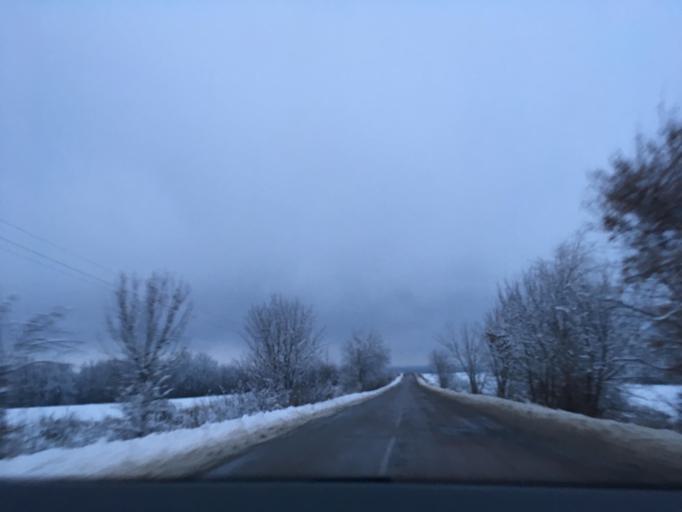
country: RU
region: Voronezj
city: Verkhniy Mamon
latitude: 50.0677
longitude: 40.2833
